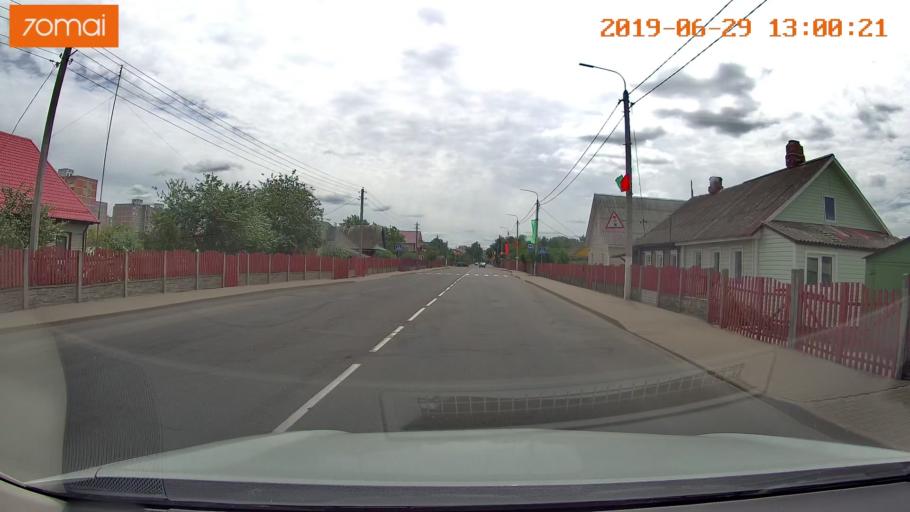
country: BY
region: Minsk
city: Slutsk
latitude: 53.0452
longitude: 27.5567
